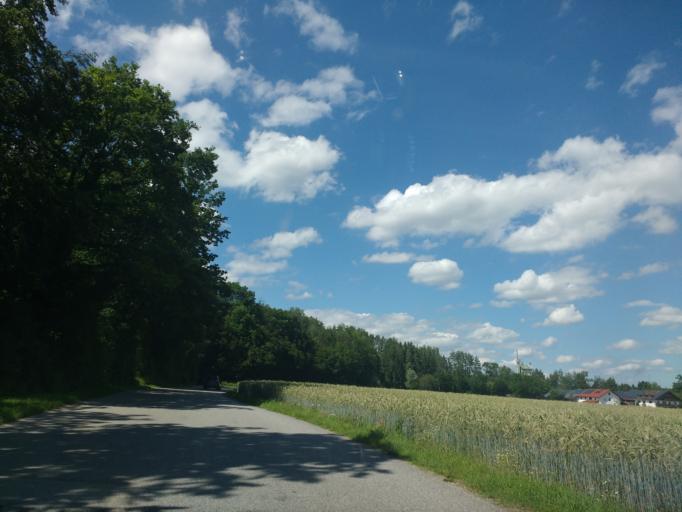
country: DE
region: Bavaria
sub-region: Upper Bavaria
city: Mehring
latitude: 48.2043
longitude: 12.7613
